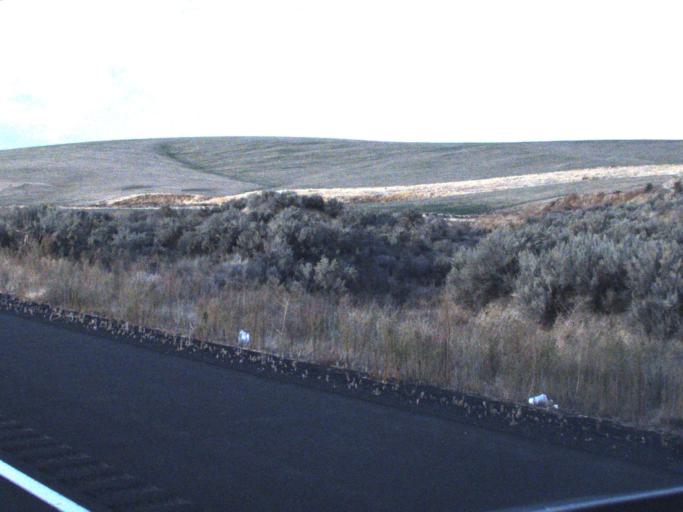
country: US
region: Washington
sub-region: Franklin County
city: Connell
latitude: 46.8771
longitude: -118.6259
